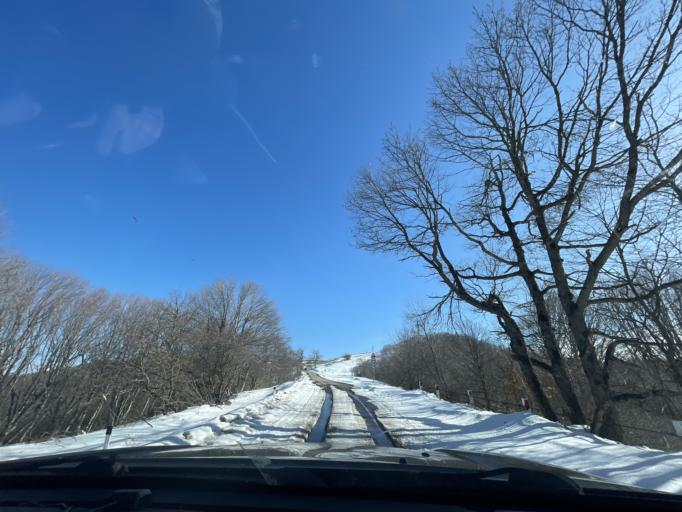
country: GE
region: Kvemo Kartli
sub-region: Tetri Tsqaro
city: Manglisi
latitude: 41.7633
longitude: 44.5062
